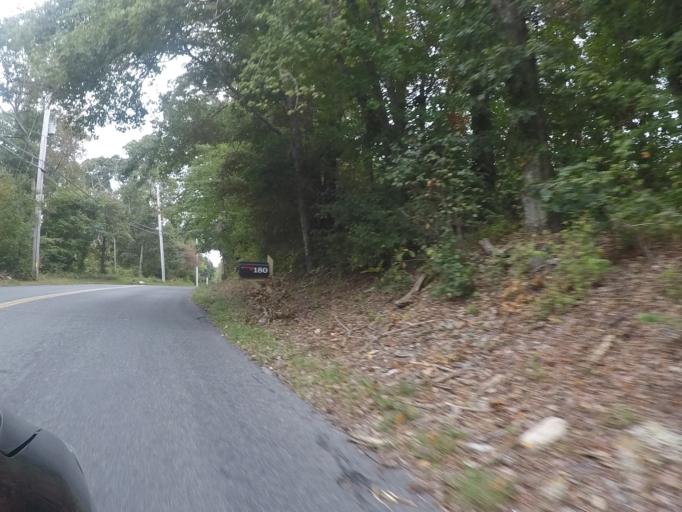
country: US
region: Massachusetts
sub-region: Bristol County
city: Smith Mills
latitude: 41.5609
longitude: -71.0079
